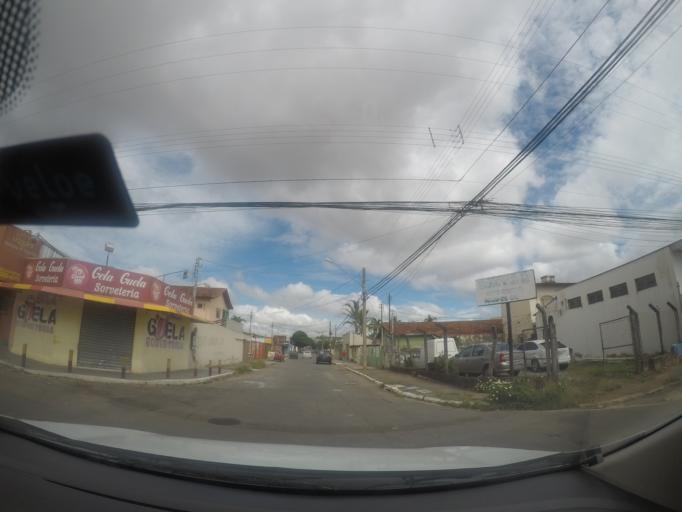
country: BR
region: Goias
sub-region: Goiania
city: Goiania
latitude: -16.6643
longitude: -49.2904
